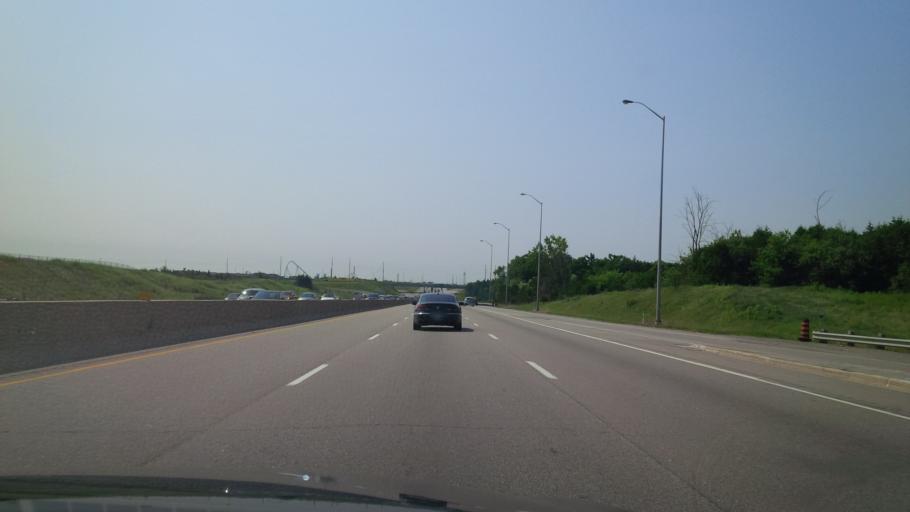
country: CA
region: Ontario
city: Vaughan
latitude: 43.8724
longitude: -79.5547
